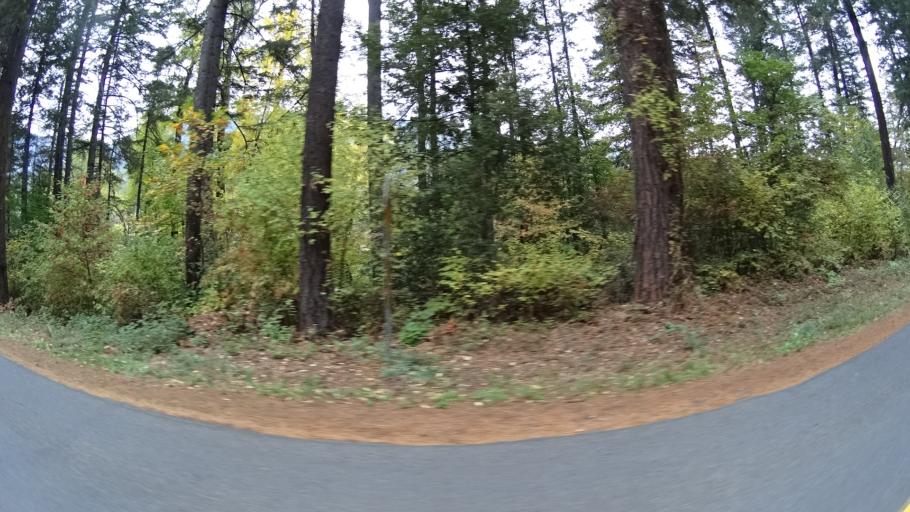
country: US
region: California
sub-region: Siskiyou County
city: Happy Camp
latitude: 41.7861
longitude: -123.3873
